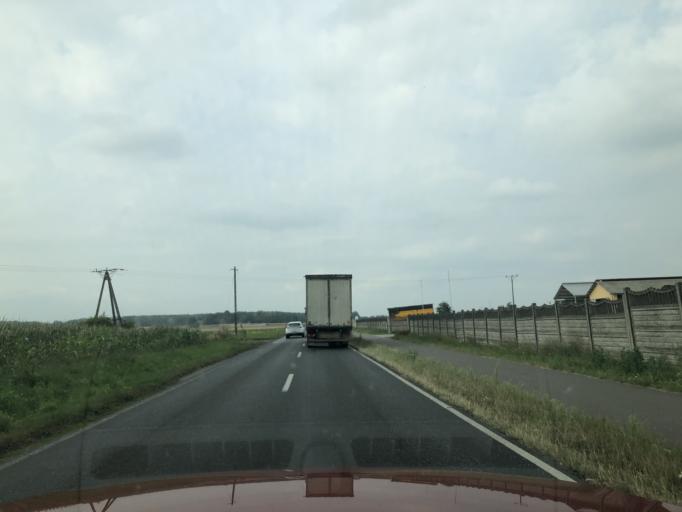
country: PL
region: Greater Poland Voivodeship
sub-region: Powiat leszczynski
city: Swieciechowa
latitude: 51.8820
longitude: 16.4462
